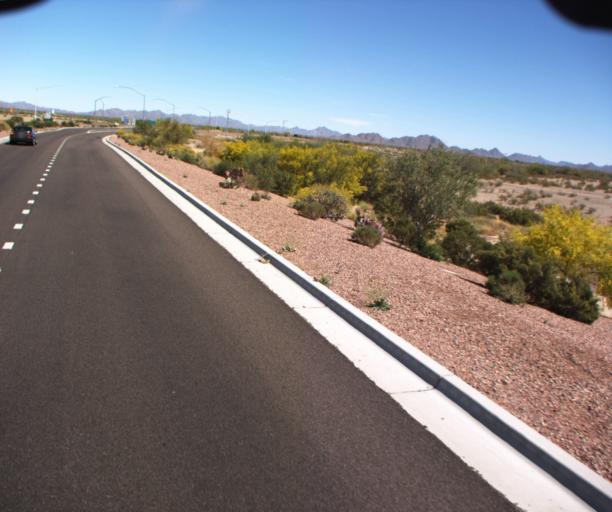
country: US
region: Arizona
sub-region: Maricopa County
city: Gila Bend
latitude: 32.9535
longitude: -112.6880
